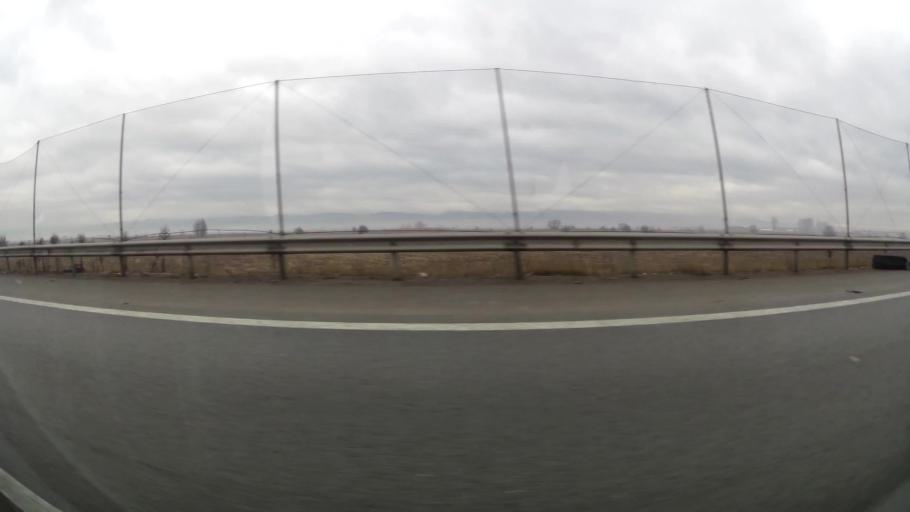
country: BG
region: Sofia-Capital
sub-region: Stolichna Obshtina
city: Sofia
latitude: 42.7177
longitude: 23.4259
